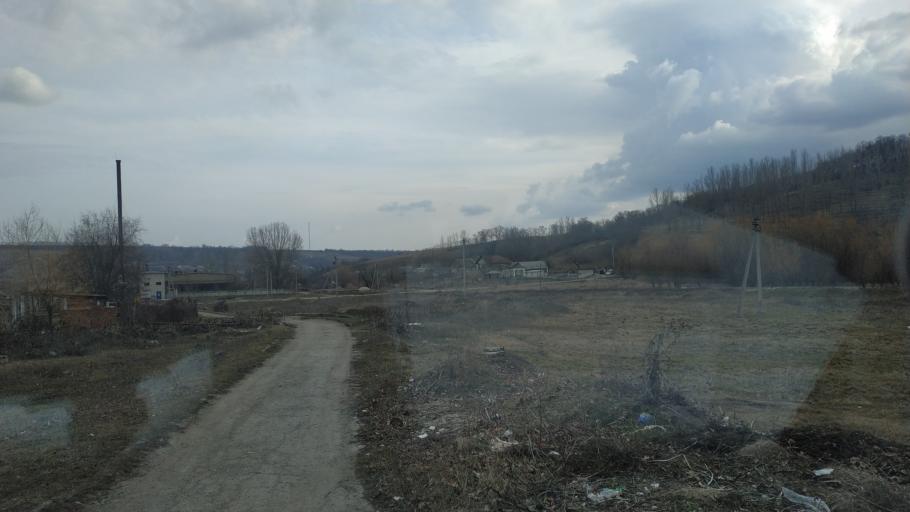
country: MD
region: Anenii Noi
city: Varnita
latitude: 46.8397
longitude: 29.3589
